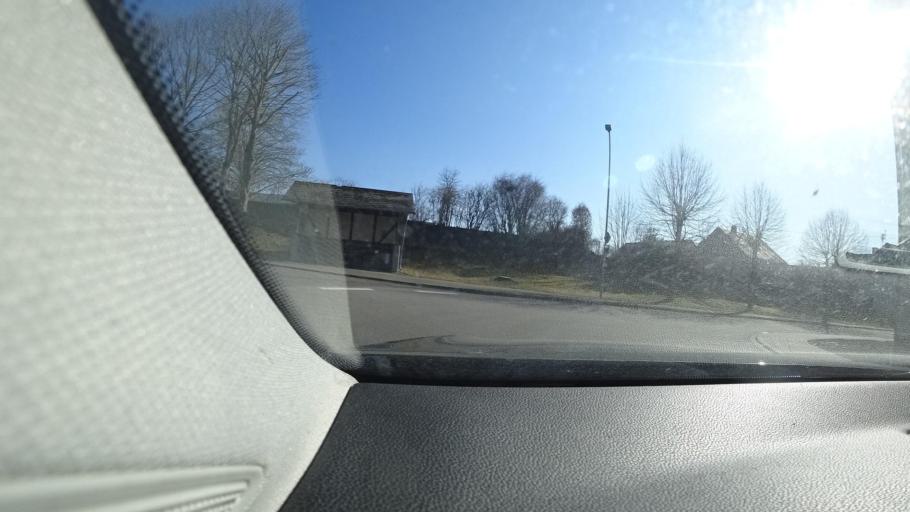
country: DE
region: Rheinland-Pfalz
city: Morschbach
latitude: 50.0116
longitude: 7.6257
